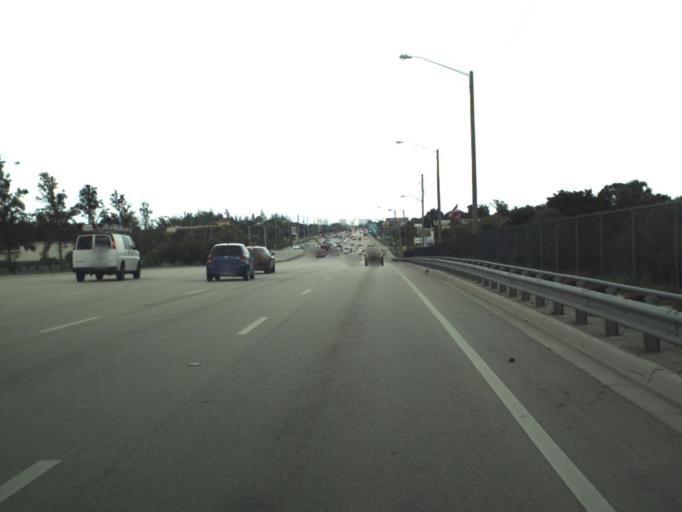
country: US
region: Florida
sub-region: Palm Beach County
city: Plantation Mobile Home Park
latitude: 26.7075
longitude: -80.1406
